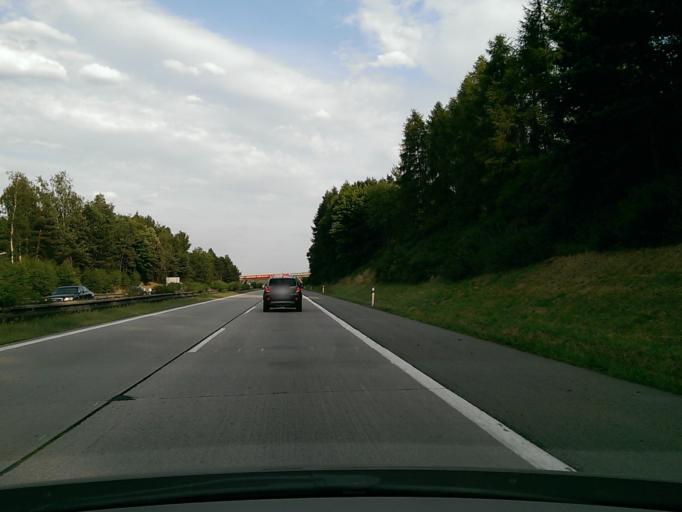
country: CZ
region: Vysocina
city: Velky Beranov
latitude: 49.4365
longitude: 15.6431
